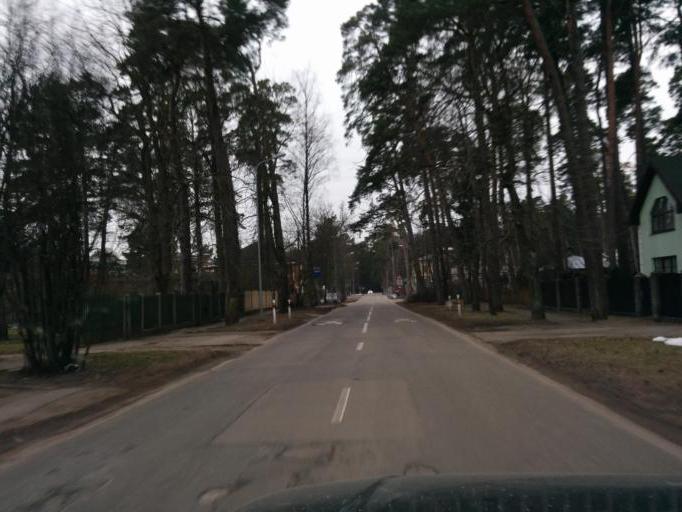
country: LV
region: Babite
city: Pinki
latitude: 56.9937
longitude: 23.9158
